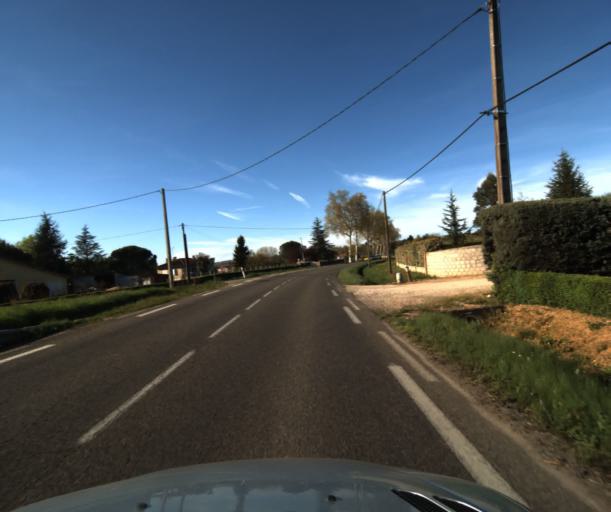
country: FR
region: Midi-Pyrenees
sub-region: Departement du Tarn-et-Garonne
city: Montbeton
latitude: 44.0672
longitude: 1.2865
